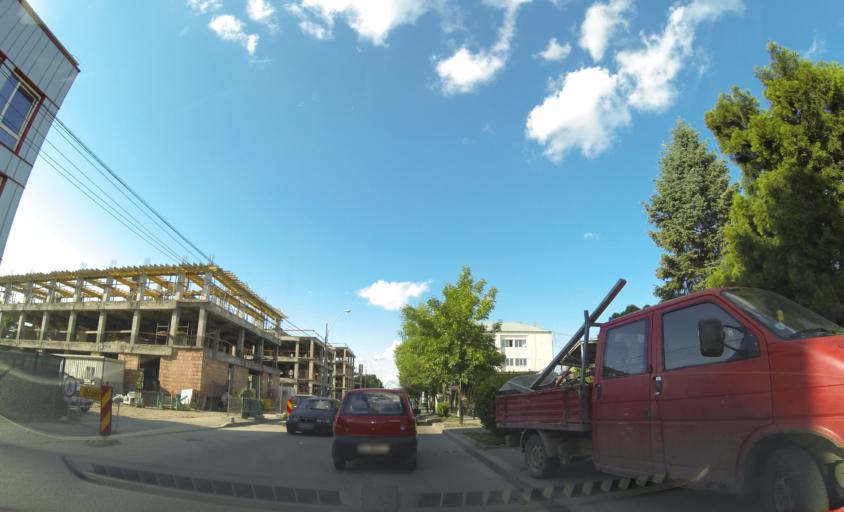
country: RO
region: Dolj
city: Craiova
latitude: 44.3127
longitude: 23.8252
